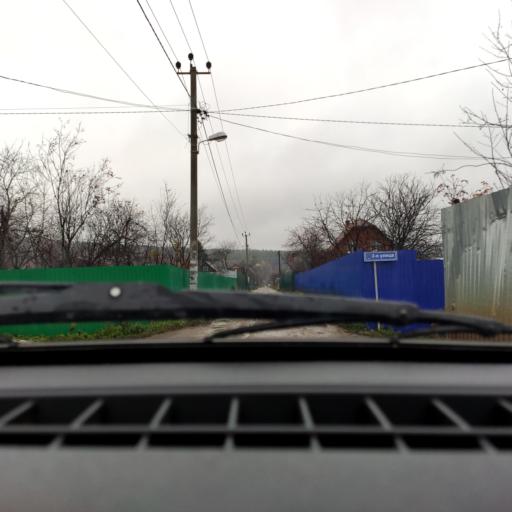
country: RU
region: Bashkortostan
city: Ufa
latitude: 54.8104
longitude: 56.1538
